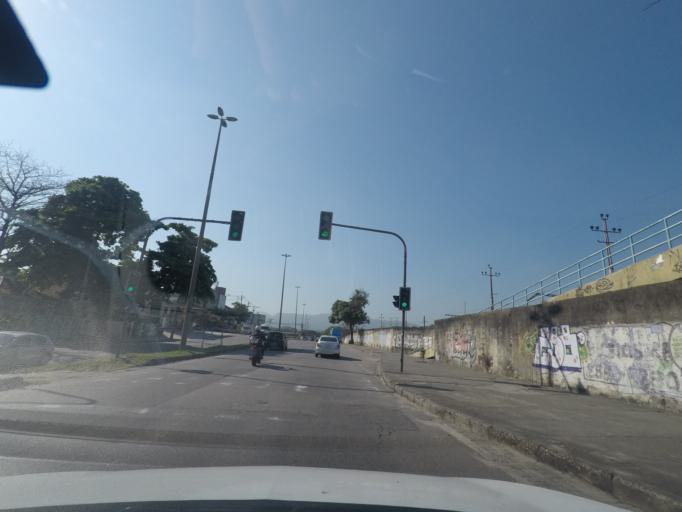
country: BR
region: Rio de Janeiro
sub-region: Rio De Janeiro
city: Rio de Janeiro
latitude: -22.8692
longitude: -43.2546
